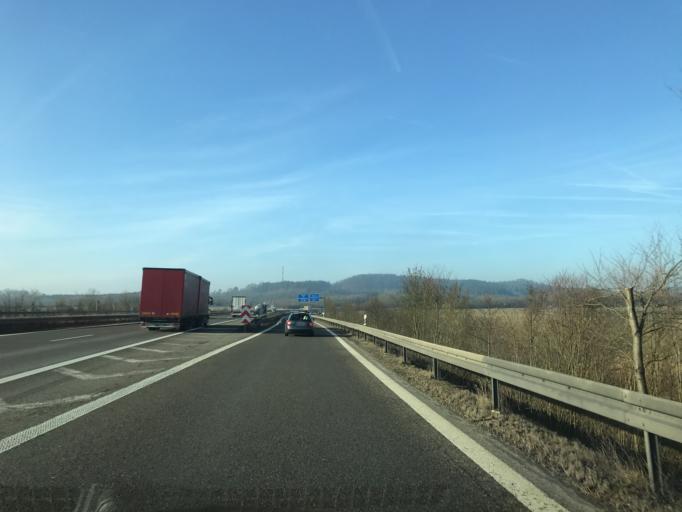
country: DE
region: Bavaria
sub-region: Regierungsbezirk Mittelfranken
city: Schnelldorf
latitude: 49.2065
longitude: 10.2448
